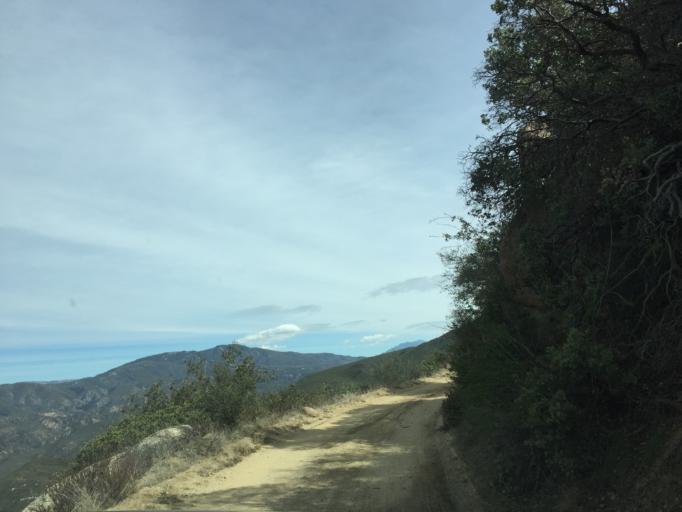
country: US
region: California
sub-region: Riverside County
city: Anza
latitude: 33.6159
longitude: -116.8088
